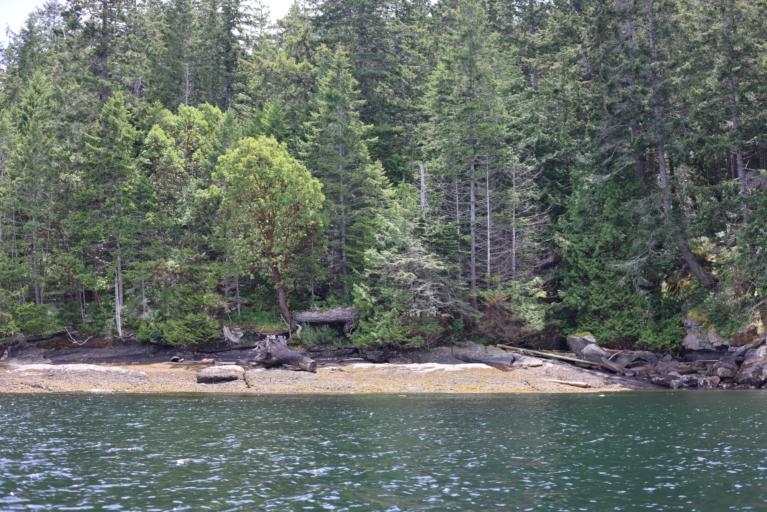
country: CA
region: British Columbia
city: Nanaimo
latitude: 49.1364
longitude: -123.8223
